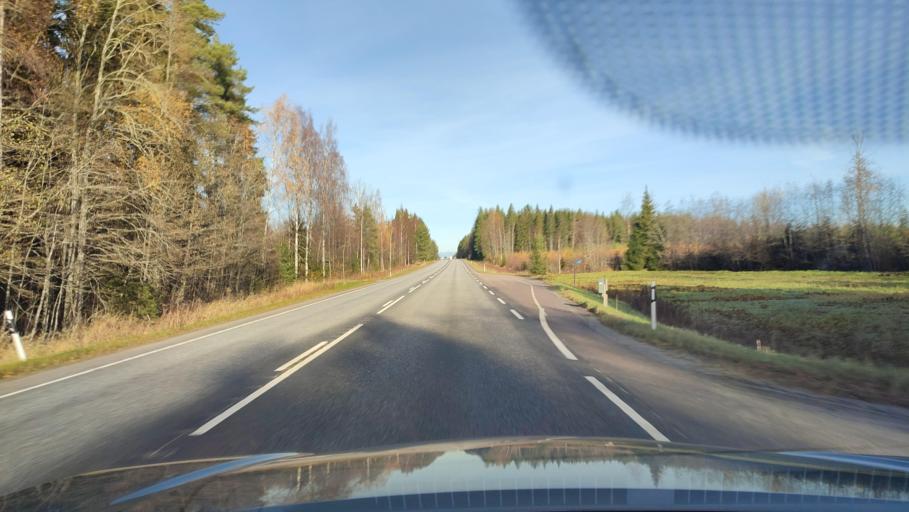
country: FI
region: Ostrobothnia
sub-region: Vaasa
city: Malax
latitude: 62.8142
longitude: 21.6843
